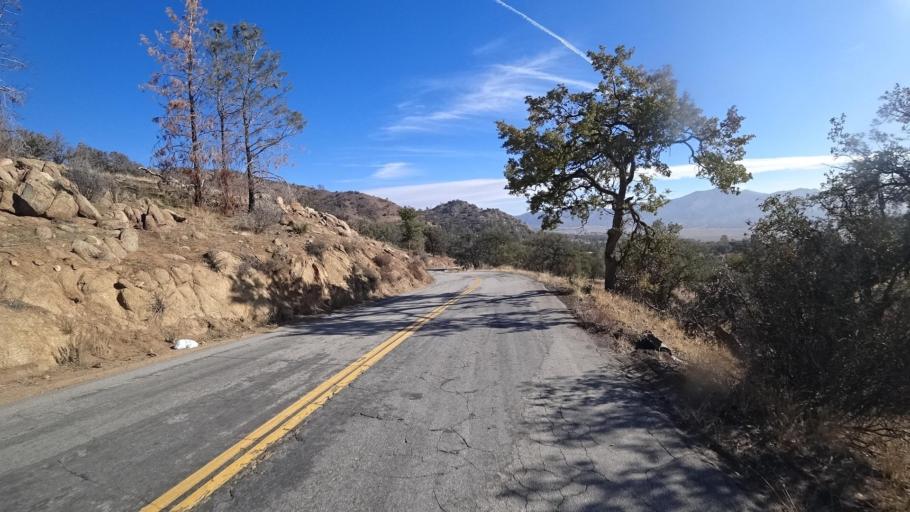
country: US
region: California
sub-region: Kern County
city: Bodfish
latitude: 35.4395
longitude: -118.5276
